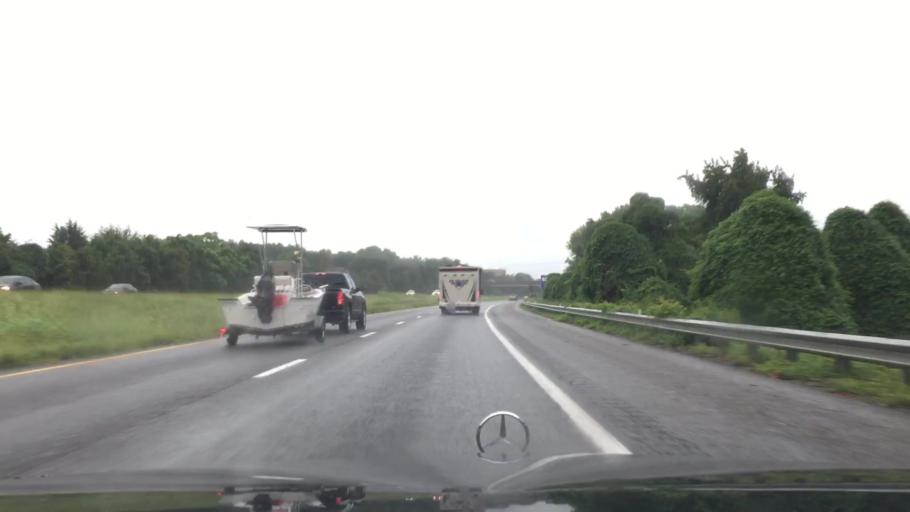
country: US
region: Virginia
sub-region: City of Charlottesville
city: Charlottesville
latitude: 38.0075
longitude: -78.4866
